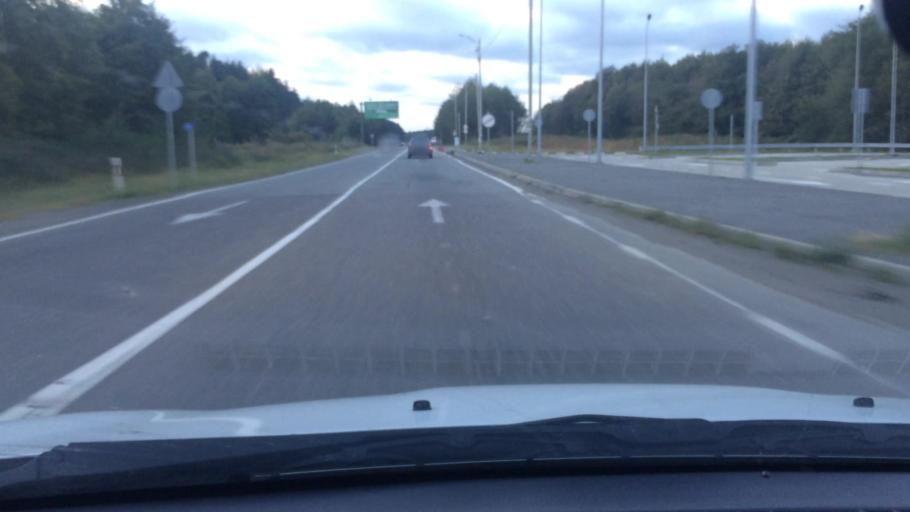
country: GE
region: Guria
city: Urek'i
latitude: 41.9401
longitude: 41.7712
